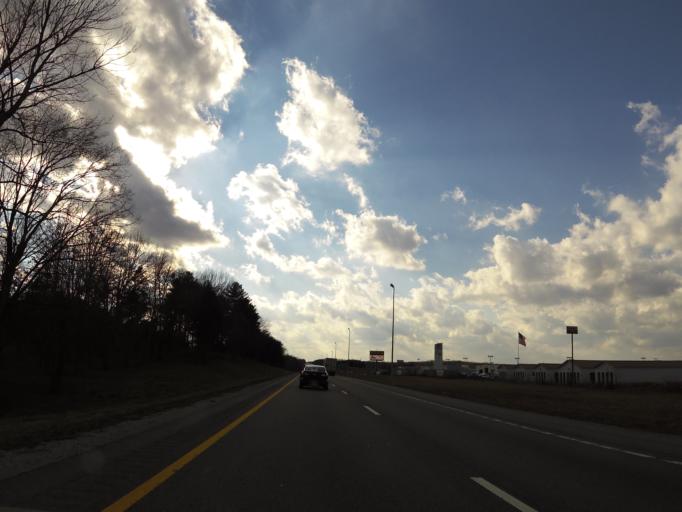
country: US
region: Tennessee
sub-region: Putnam County
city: Cookeville
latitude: 36.1369
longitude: -85.5195
